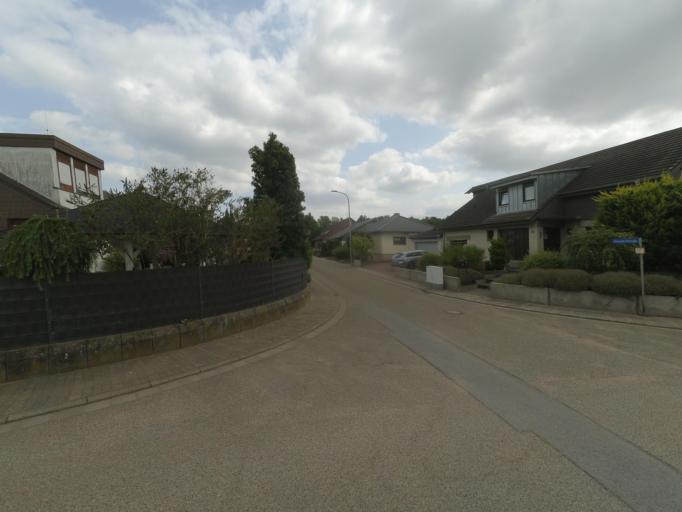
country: DE
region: Rheinland-Pfalz
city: Hanhofen
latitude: 49.3134
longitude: 8.3492
